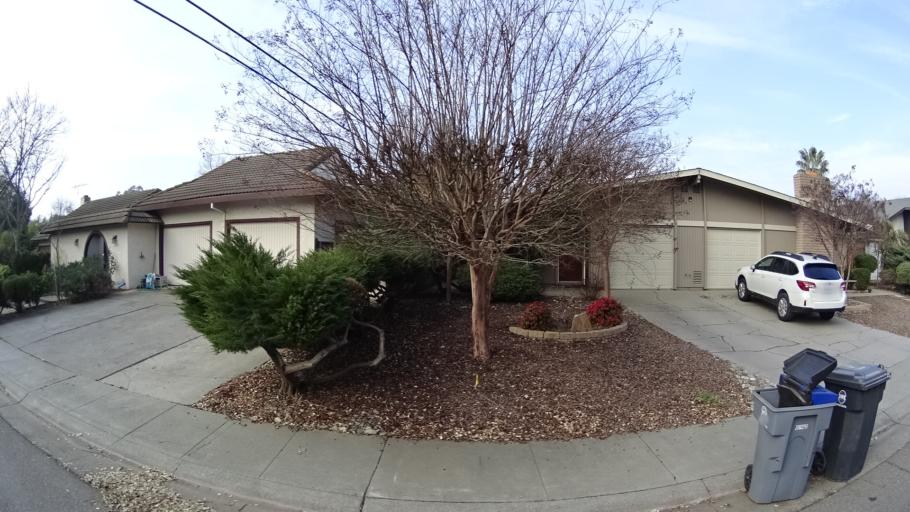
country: US
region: California
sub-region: Yolo County
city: Davis
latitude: 38.5576
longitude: -121.7566
